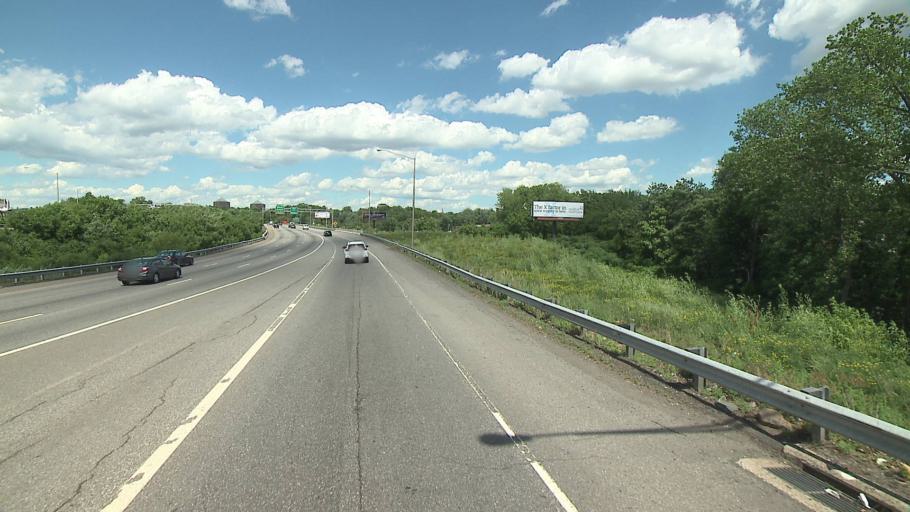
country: US
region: Connecticut
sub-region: Hartford County
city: Hartford
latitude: 41.7501
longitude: -72.7042
